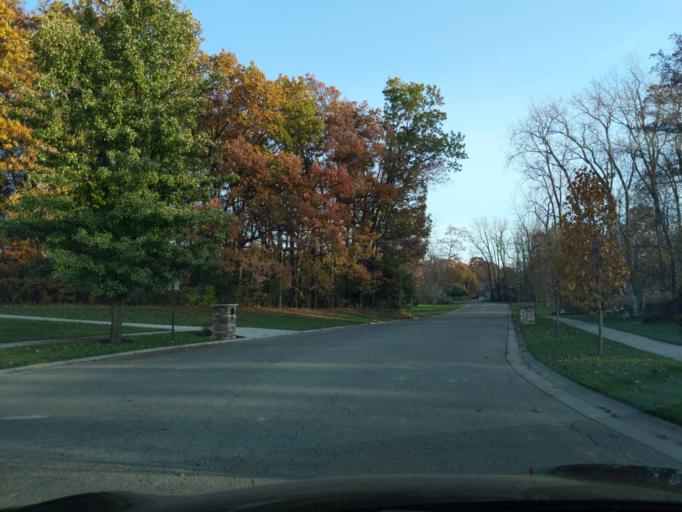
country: US
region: Michigan
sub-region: Clinton County
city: Bath
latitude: 42.7992
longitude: -84.4635
